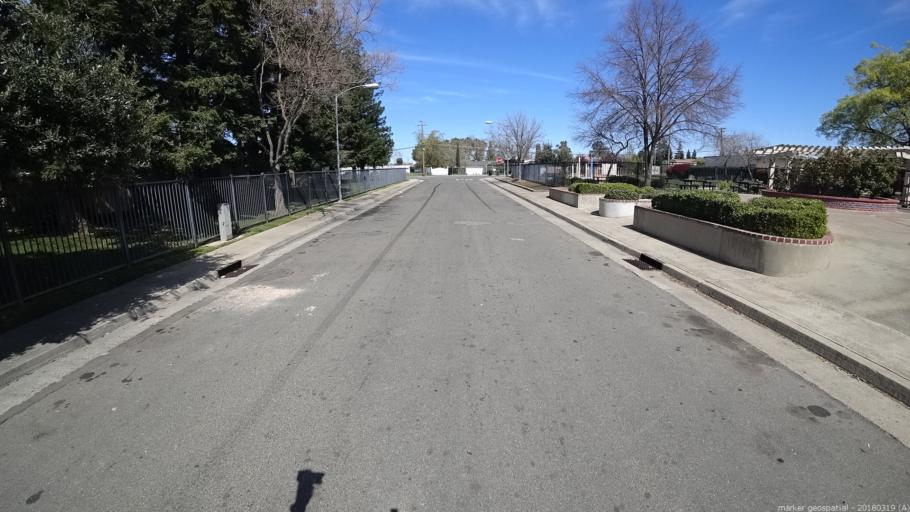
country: US
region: California
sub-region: Sacramento County
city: Parkway
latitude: 38.5132
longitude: -121.4468
